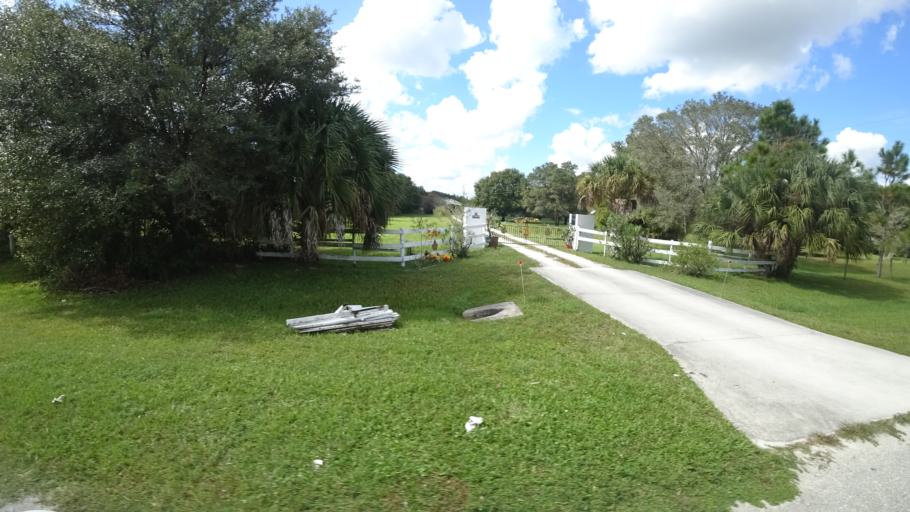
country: US
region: Florida
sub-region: Sarasota County
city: Lake Sarasota
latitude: 27.2860
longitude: -82.2303
